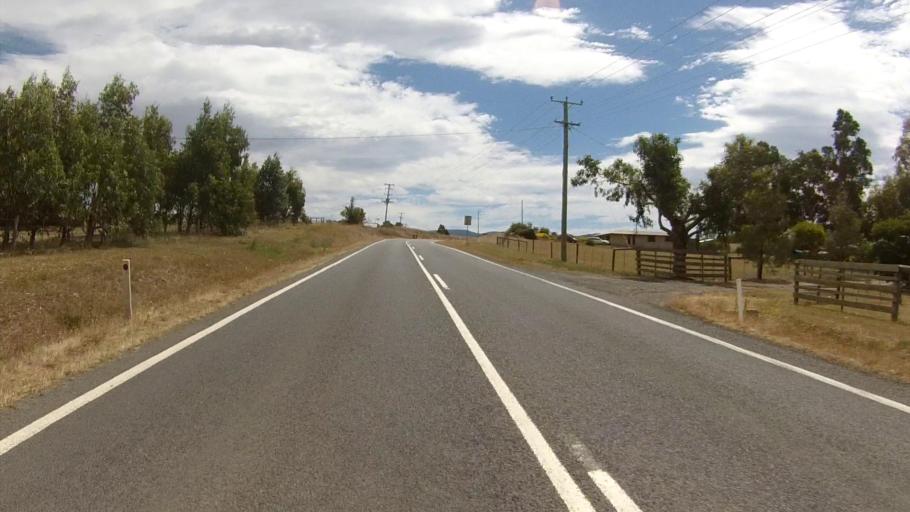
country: AU
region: Tasmania
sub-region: Brighton
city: Bridgewater
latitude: -42.6983
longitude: 147.2692
